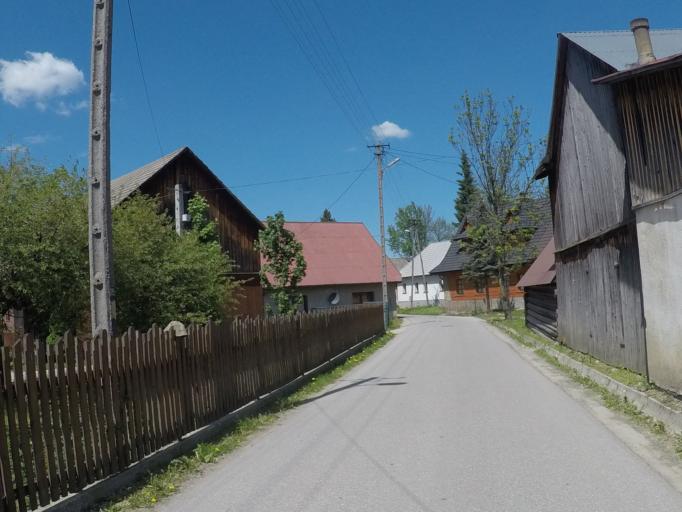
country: PL
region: Lesser Poland Voivodeship
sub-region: Powiat tatrzanski
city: Bukowina Tatrzanska
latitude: 49.3398
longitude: 20.1366
